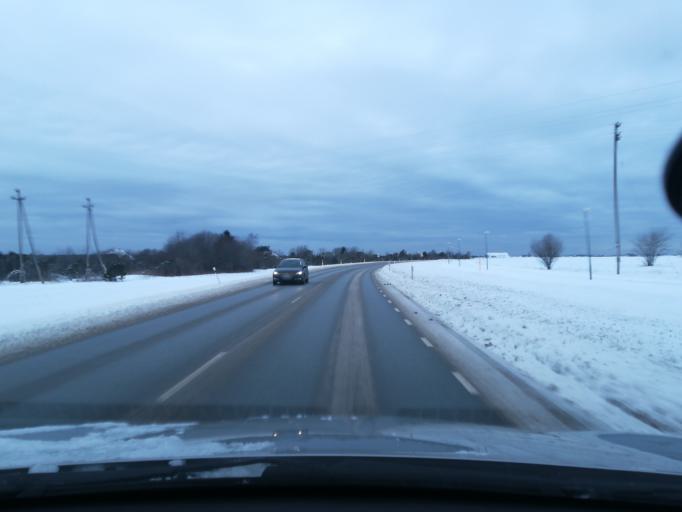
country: EE
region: Harju
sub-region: Harku vald
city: Tabasalu
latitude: 59.4430
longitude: 24.4872
